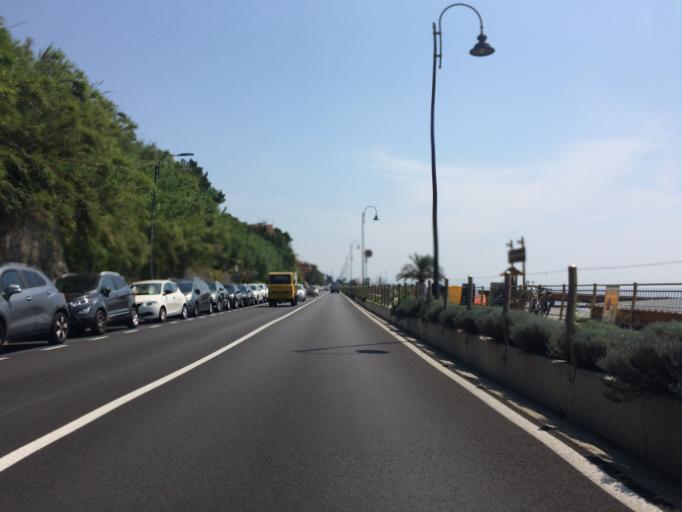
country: IT
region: Liguria
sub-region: Provincia di Genova
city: Cogoleto
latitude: 44.3908
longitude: 8.6556
